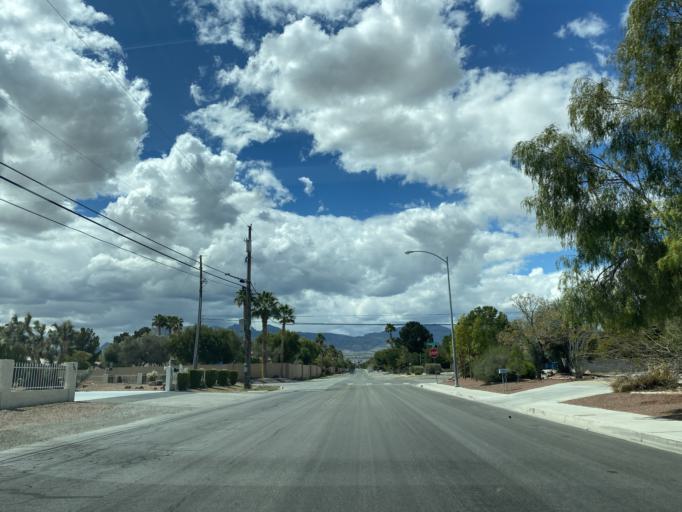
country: US
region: Nevada
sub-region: Clark County
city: Spring Valley
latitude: 36.2444
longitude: -115.2690
